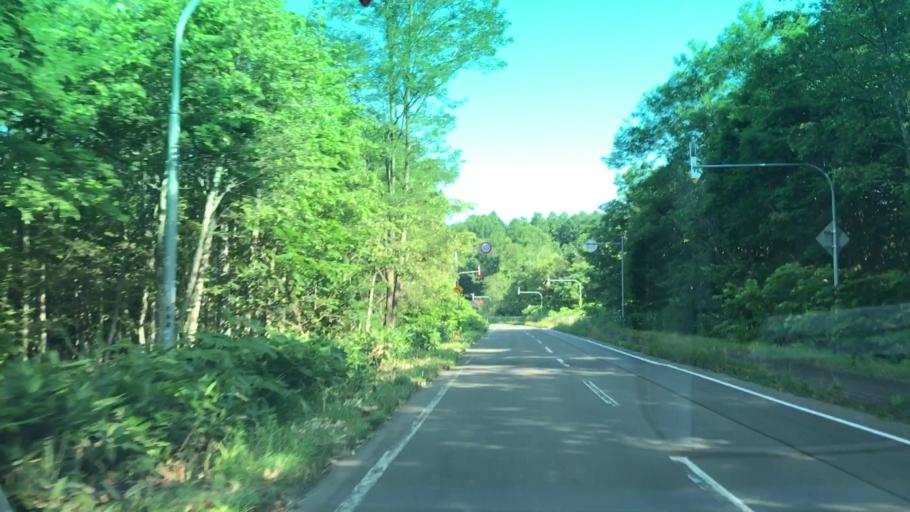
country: JP
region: Hokkaido
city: Yoichi
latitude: 43.0661
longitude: 140.7064
